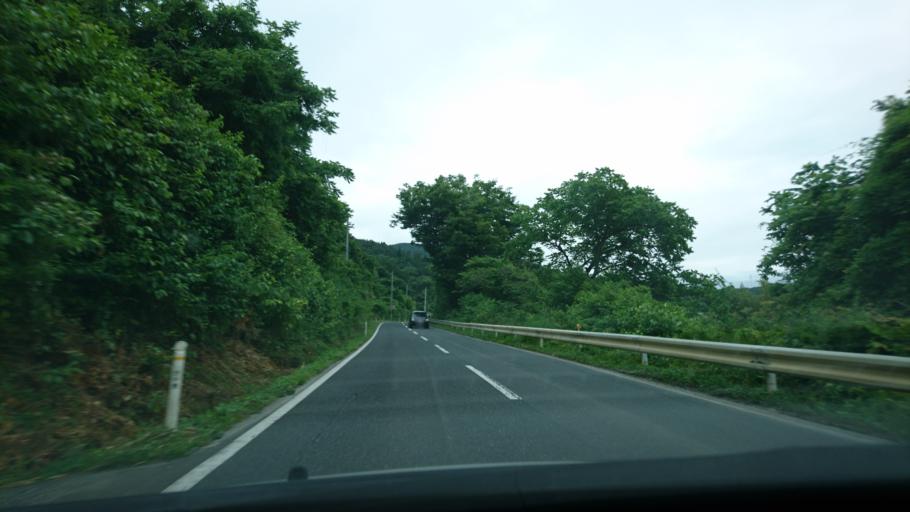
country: JP
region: Iwate
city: Ichinoseki
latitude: 38.9719
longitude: 141.2386
